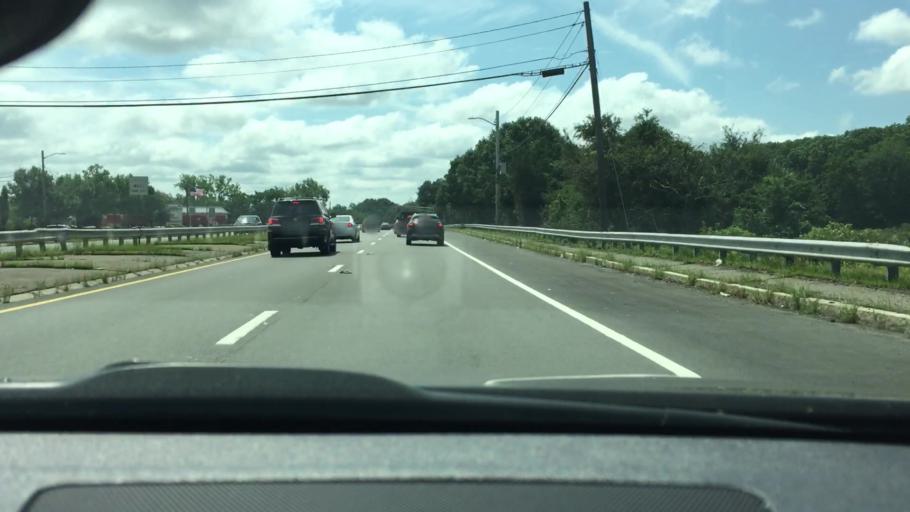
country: US
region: Massachusetts
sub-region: Norfolk County
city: Dedham
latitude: 42.2582
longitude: -71.1702
